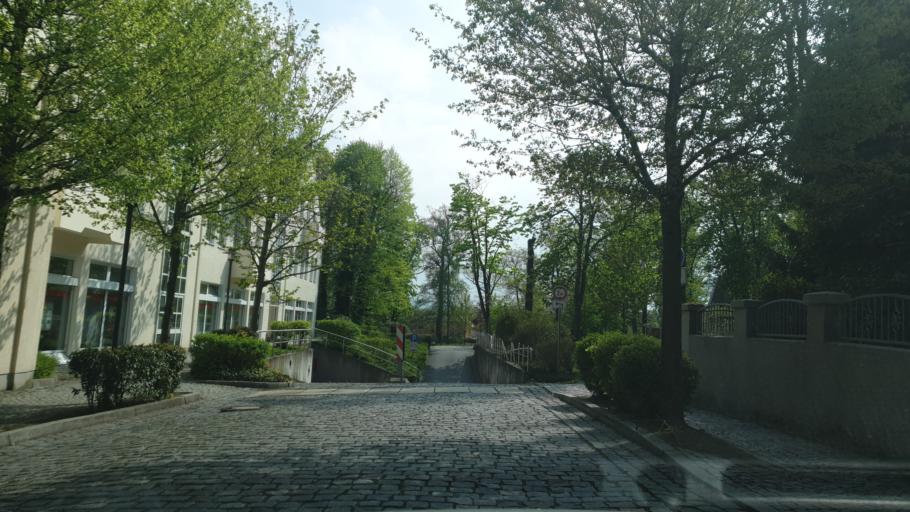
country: DE
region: Saxony
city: Stollberg
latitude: 50.7085
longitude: 12.7771
